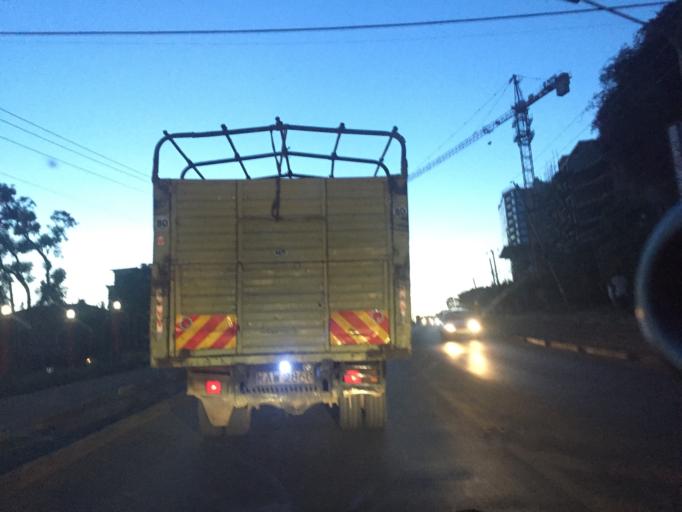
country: KE
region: Nairobi Area
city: Nairobi
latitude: -1.2900
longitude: 36.7775
